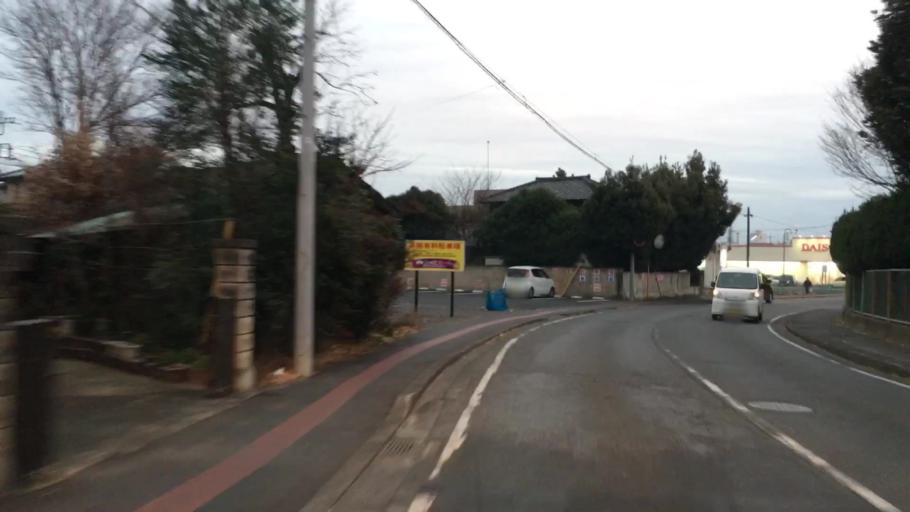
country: JP
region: Gunma
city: Ota
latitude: 36.3005
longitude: 139.3670
